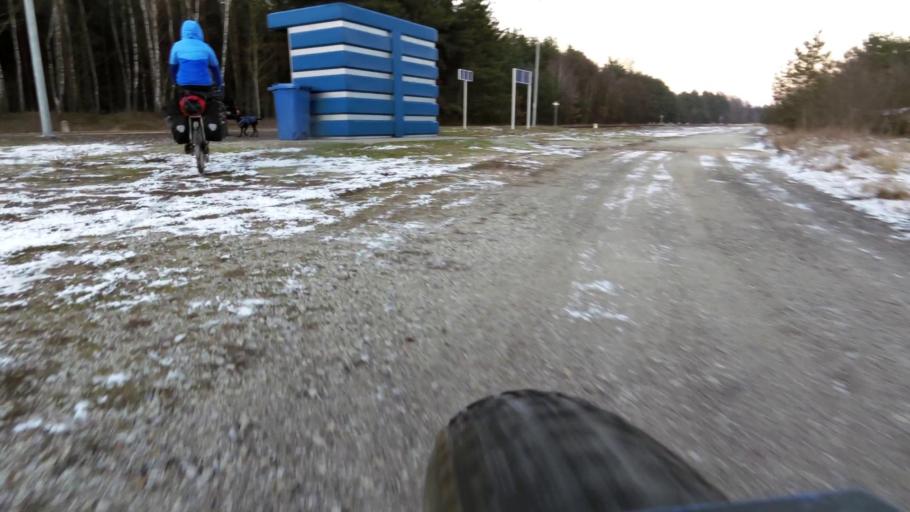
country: PL
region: West Pomeranian Voivodeship
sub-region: Powiat walecki
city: Walcz
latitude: 53.2436
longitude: 16.3619
